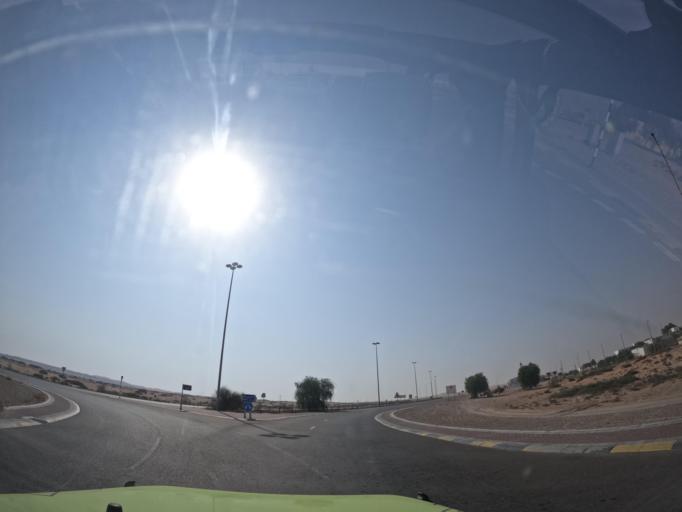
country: OM
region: Al Buraimi
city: Al Buraymi
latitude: 24.5241
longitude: 55.5529
